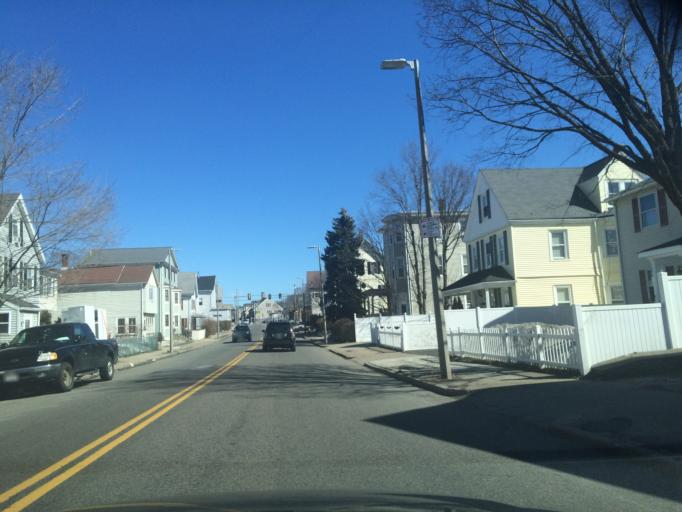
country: US
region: Massachusetts
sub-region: Norfolk County
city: Dedham
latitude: 42.2474
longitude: -71.1278
